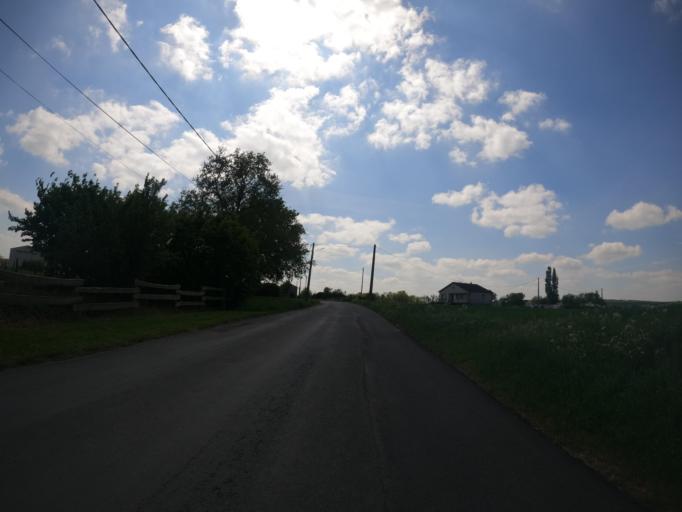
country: FR
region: Poitou-Charentes
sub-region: Departement des Deux-Sevres
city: Saint-Varent
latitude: 46.8569
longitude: -0.2543
